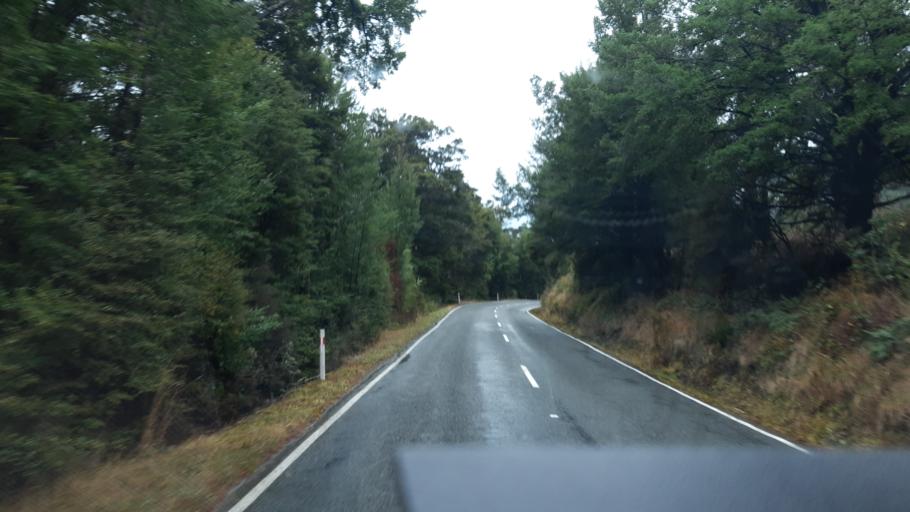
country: NZ
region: Tasman
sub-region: Tasman District
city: Wakefield
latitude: -41.7560
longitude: 172.8968
